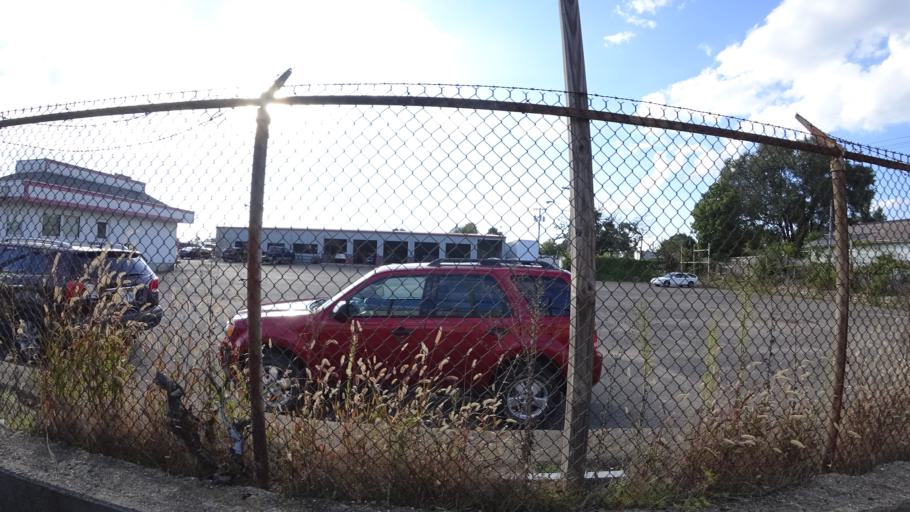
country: US
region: Michigan
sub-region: Saint Joseph County
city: Sturgis
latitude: 41.7986
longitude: -85.4300
